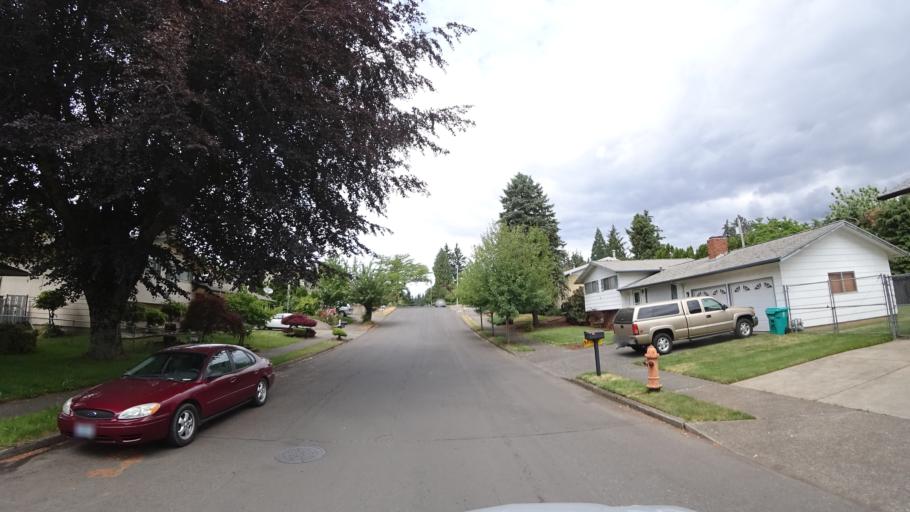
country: US
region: Oregon
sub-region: Multnomah County
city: Lents
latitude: 45.5003
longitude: -122.5184
